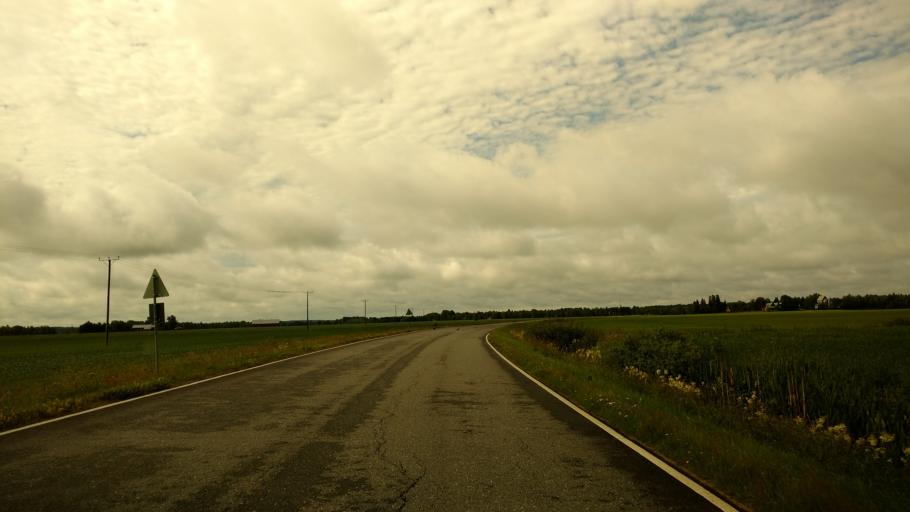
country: FI
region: Varsinais-Suomi
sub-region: Loimaa
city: Koski Tl
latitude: 60.6746
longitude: 23.1603
